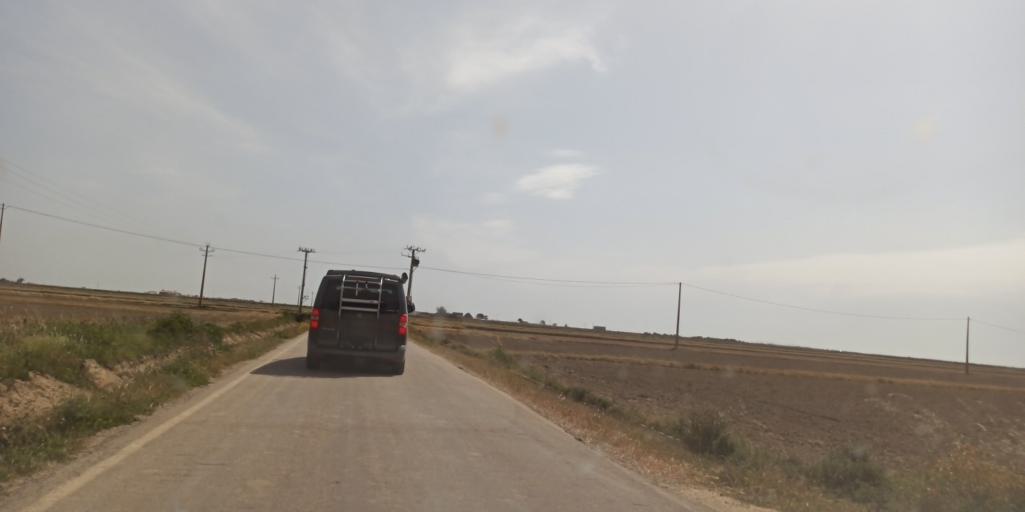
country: ES
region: Catalonia
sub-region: Provincia de Tarragona
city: Deltebre
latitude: 40.6451
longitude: 0.7226
